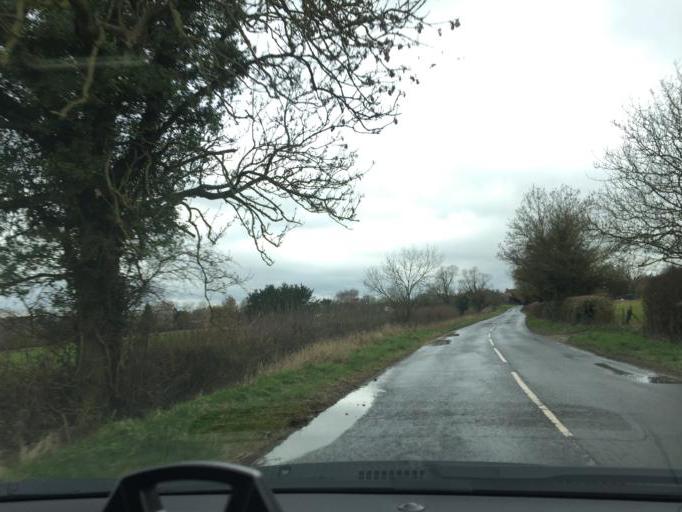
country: GB
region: England
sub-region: Northamptonshire
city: Brackley
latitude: 52.0938
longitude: -1.1314
